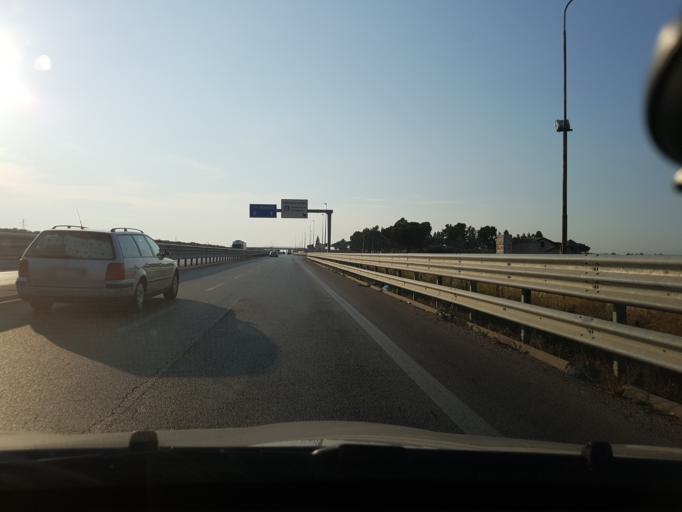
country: IT
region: Apulia
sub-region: Provincia di Foggia
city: Stornara
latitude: 41.3061
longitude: 15.8091
